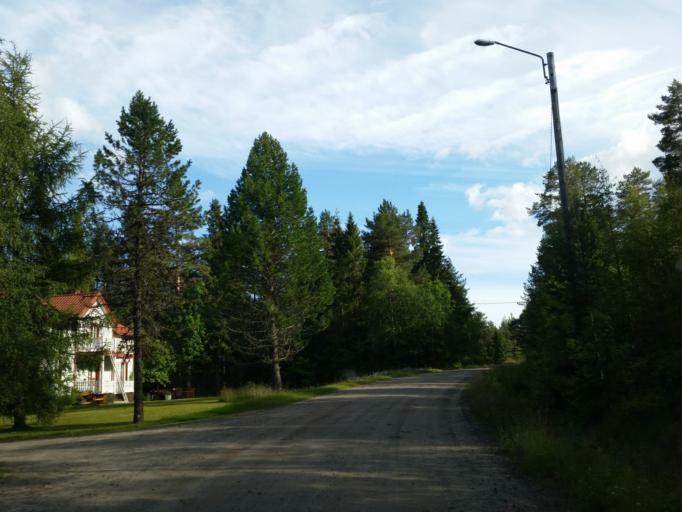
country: SE
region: Vaesterbotten
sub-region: Robertsfors Kommun
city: Robertsfors
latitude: 64.0413
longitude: 20.8499
